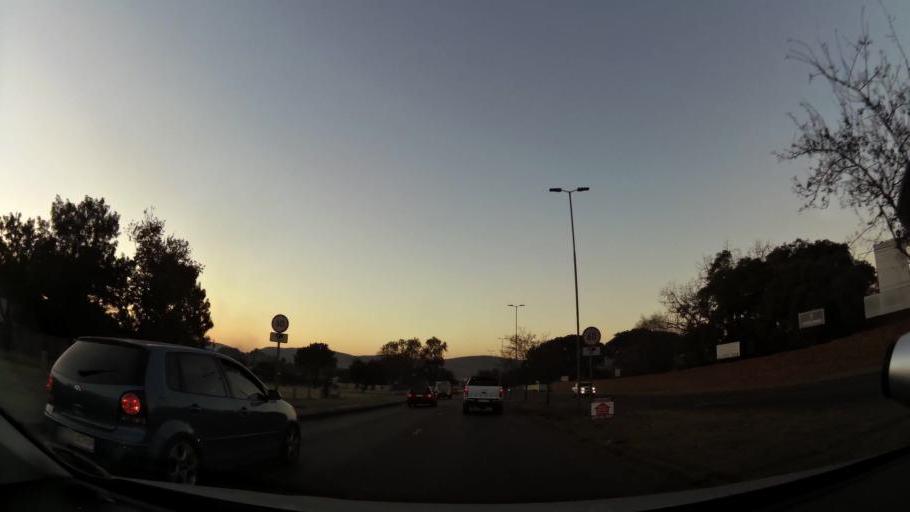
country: ZA
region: Gauteng
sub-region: City of Tshwane Metropolitan Municipality
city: Pretoria
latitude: -25.7212
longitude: 28.1354
